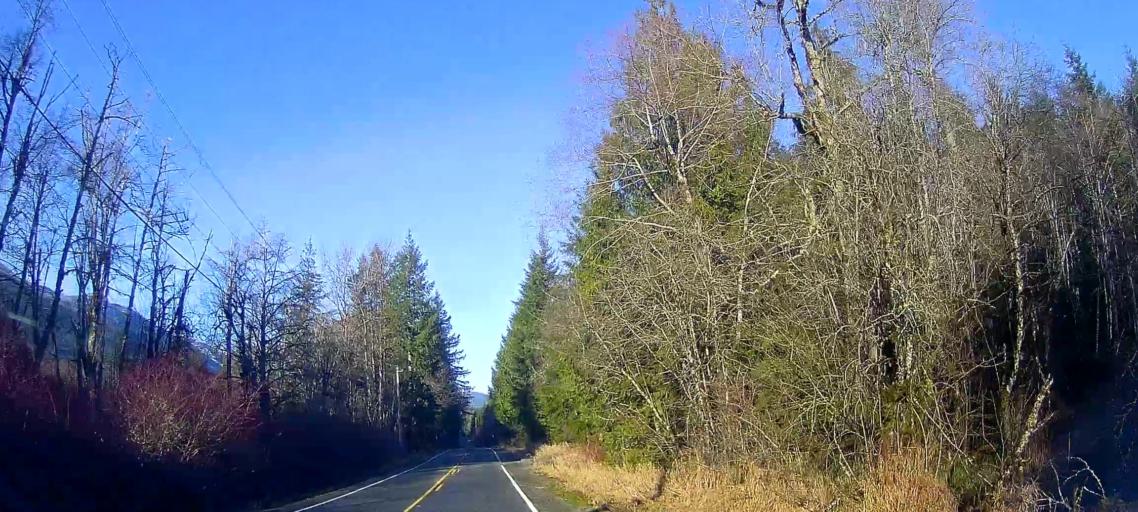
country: US
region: Washington
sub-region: Snohomish County
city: Darrington
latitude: 48.5572
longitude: -121.7658
